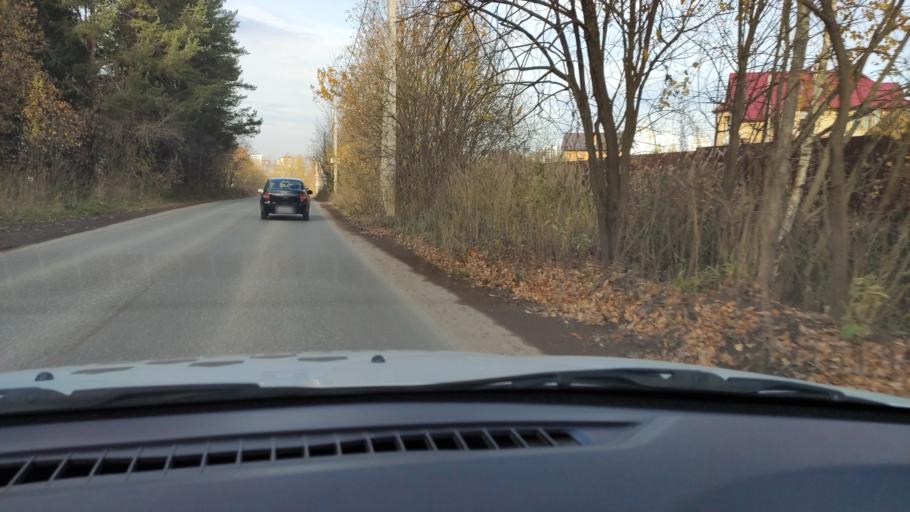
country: RU
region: Perm
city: Perm
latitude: 57.9973
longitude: 56.3306
